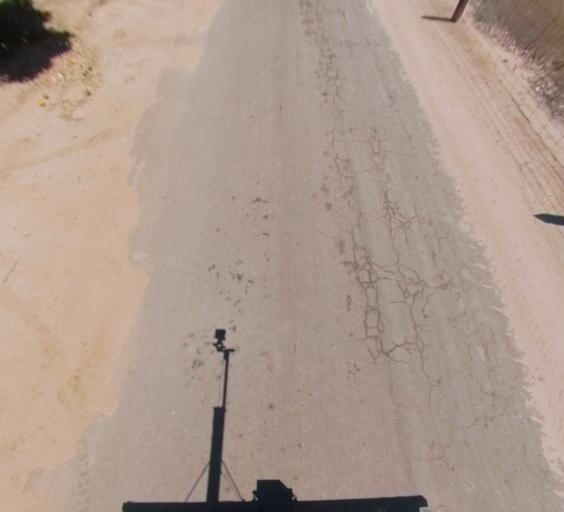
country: US
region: California
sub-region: Madera County
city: Bonadelle Ranchos-Madera Ranchos
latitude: 36.8858
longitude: -119.8214
